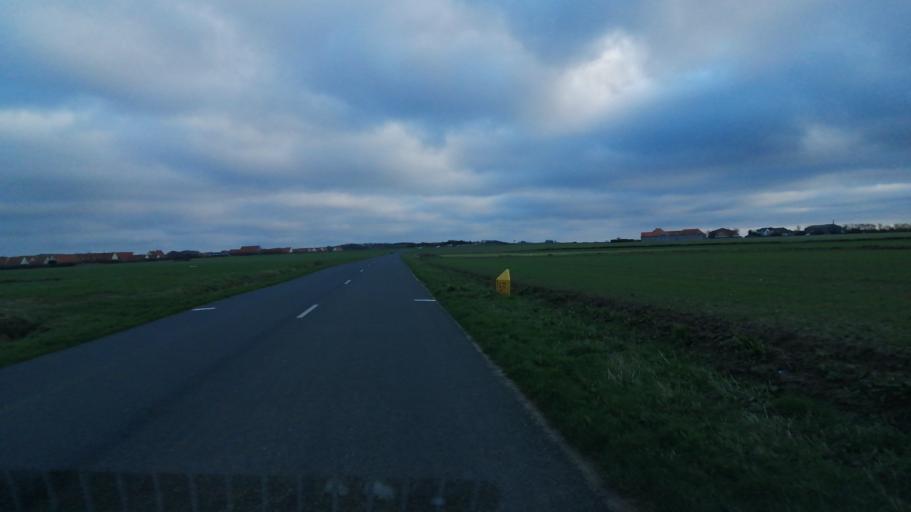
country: FR
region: Nord-Pas-de-Calais
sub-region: Departement du Pas-de-Calais
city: Ambleteuse
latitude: 50.8503
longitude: 1.5997
